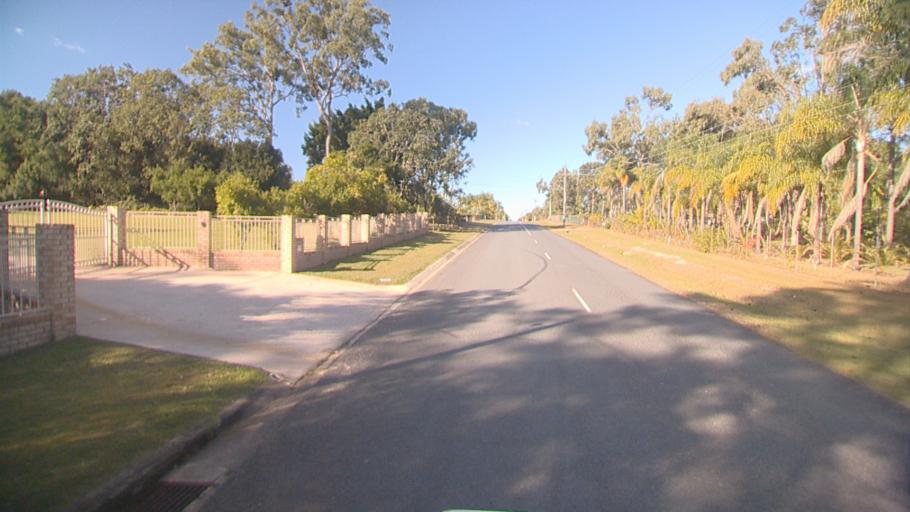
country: AU
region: Queensland
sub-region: Logan
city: Park Ridge South
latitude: -27.7083
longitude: 153.0124
